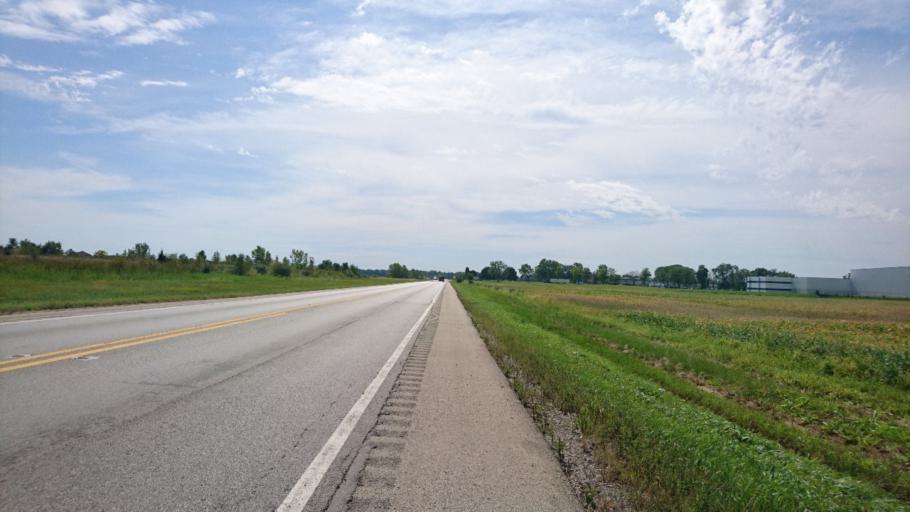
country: US
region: Illinois
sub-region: Will County
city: Wilmington
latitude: 41.3245
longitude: -88.1328
